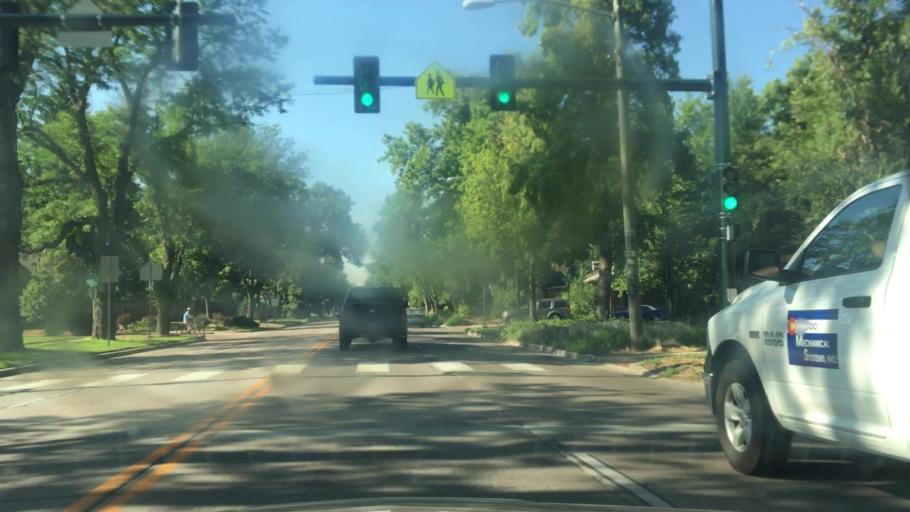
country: US
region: Colorado
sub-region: Arapahoe County
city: Glendale
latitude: 39.6953
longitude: -104.9593
